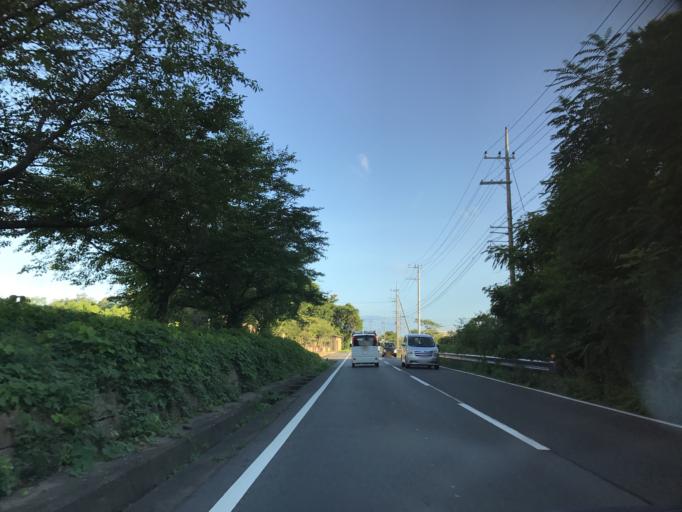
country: JP
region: Shiga Prefecture
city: Youkaichi
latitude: 35.1176
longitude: 136.2568
